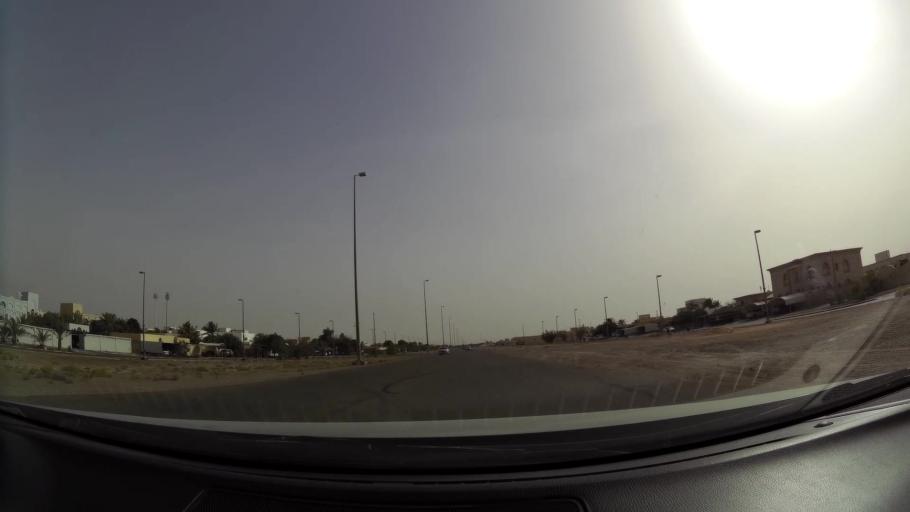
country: AE
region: Abu Dhabi
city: Al Ain
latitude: 24.2122
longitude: 55.5935
